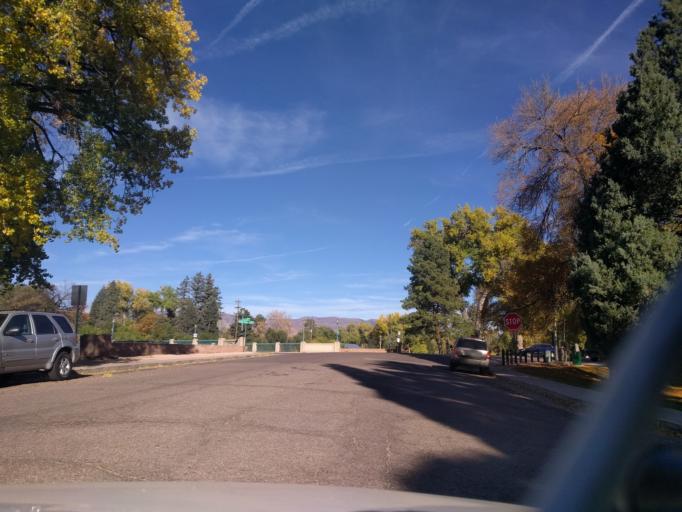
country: US
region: Colorado
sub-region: El Paso County
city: Colorado Springs
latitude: 38.8456
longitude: -104.8281
